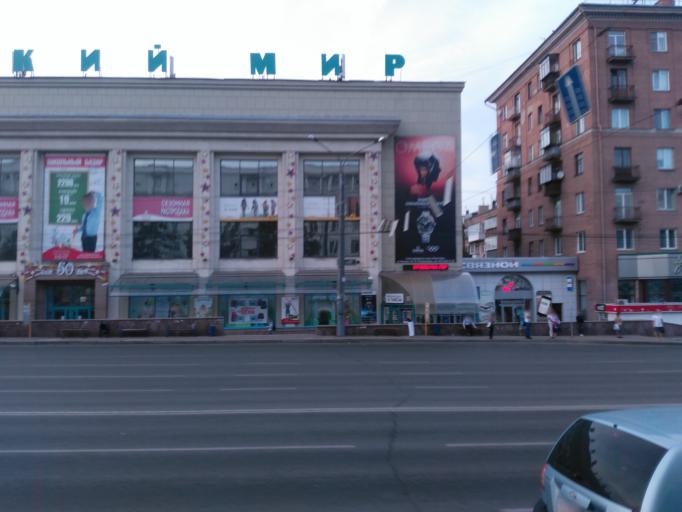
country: RU
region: Chelyabinsk
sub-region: Gorod Chelyabinsk
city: Chelyabinsk
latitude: 55.1606
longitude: 61.4103
